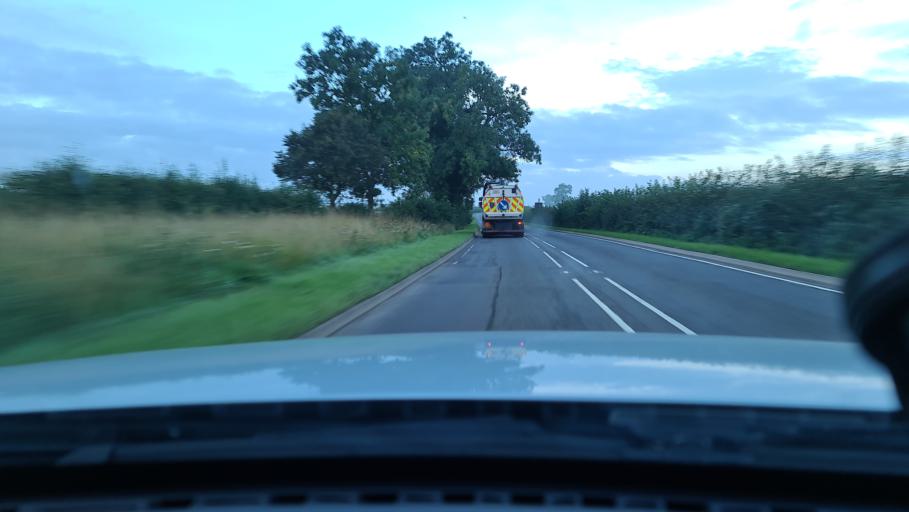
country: GB
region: England
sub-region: Warwickshire
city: Wolston
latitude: 52.3752
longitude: -1.3800
